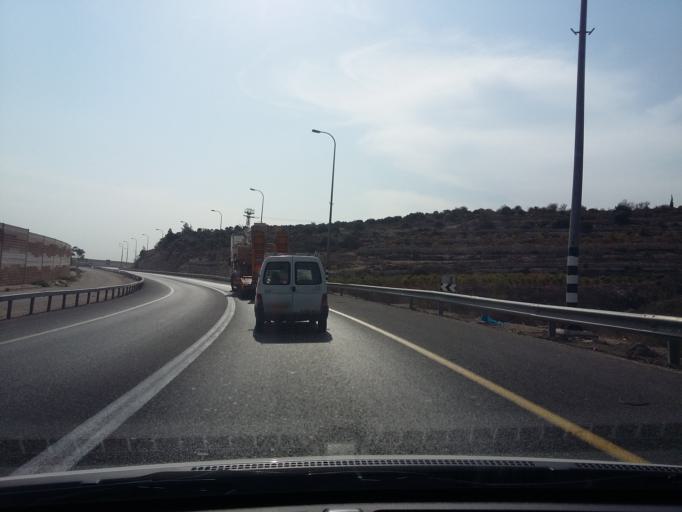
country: PS
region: West Bank
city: Al Khadir
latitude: 31.6943
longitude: 35.1564
